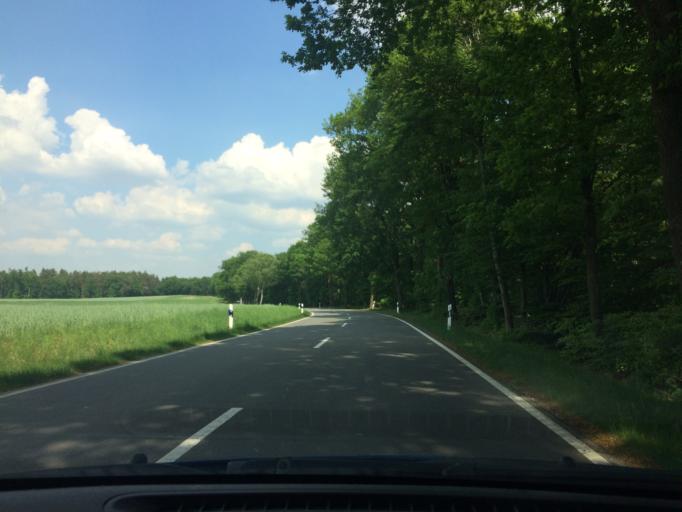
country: DE
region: Lower Saxony
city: Neu Darchau
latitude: 53.2200
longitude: 10.8595
